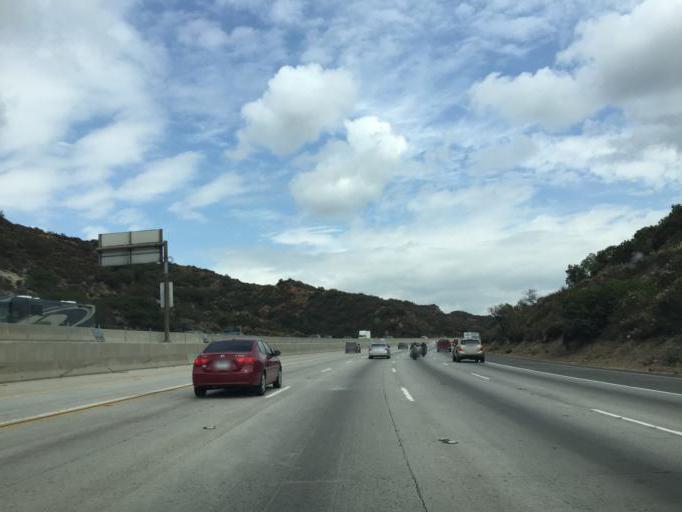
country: US
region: California
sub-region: Los Angeles County
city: La Canada Flintridge
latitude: 34.1478
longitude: -118.2003
